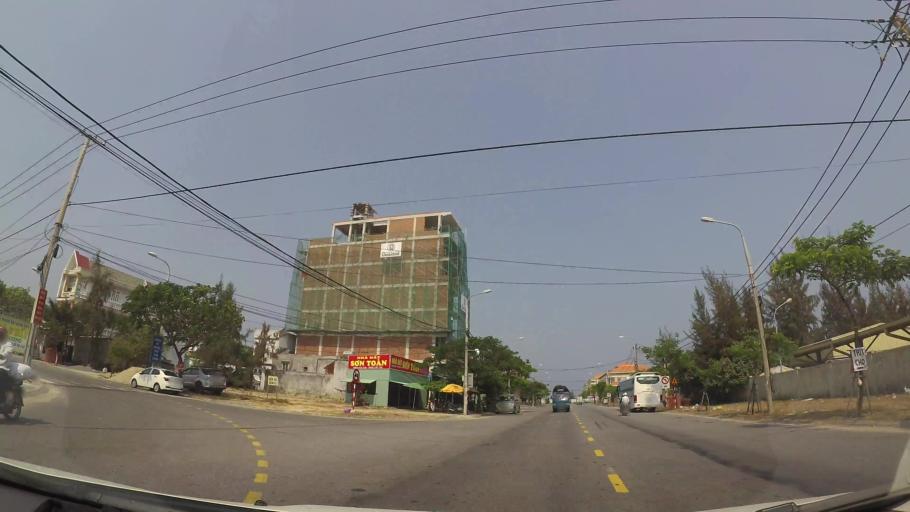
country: VN
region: Da Nang
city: Ngu Hanh Son
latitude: 15.9801
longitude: 108.2742
